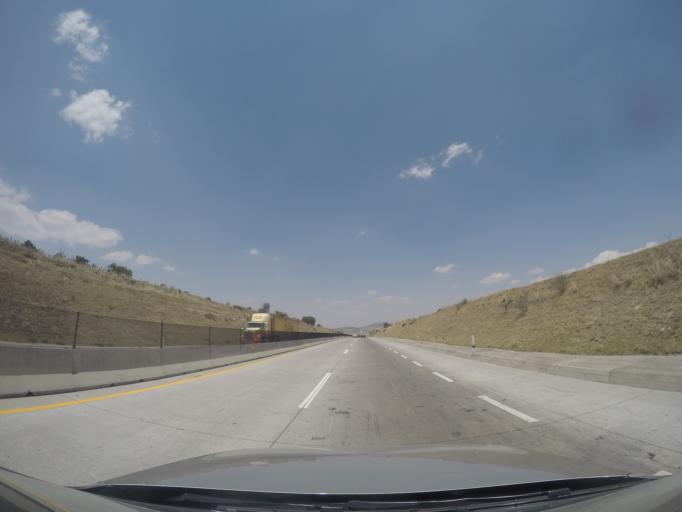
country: MX
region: Morelos
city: Jaltepec
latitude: 19.7236
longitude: -98.6112
